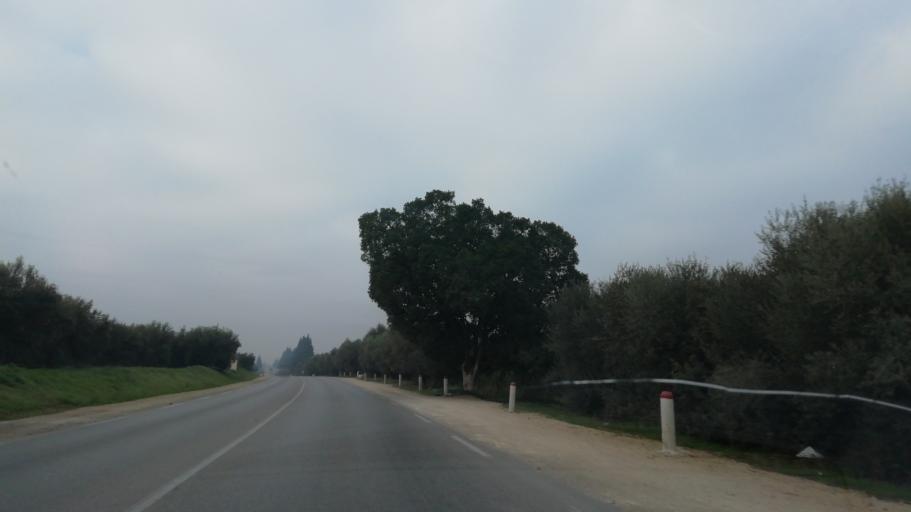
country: DZ
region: Relizane
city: Oued Rhiou
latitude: 35.9488
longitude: 0.8766
